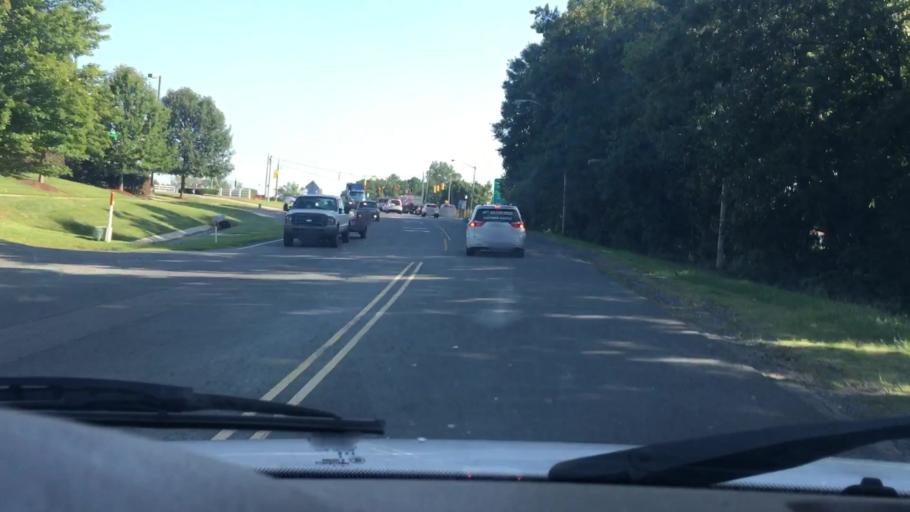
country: US
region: North Carolina
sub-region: Mecklenburg County
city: Cornelius
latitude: 35.4822
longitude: -80.8726
